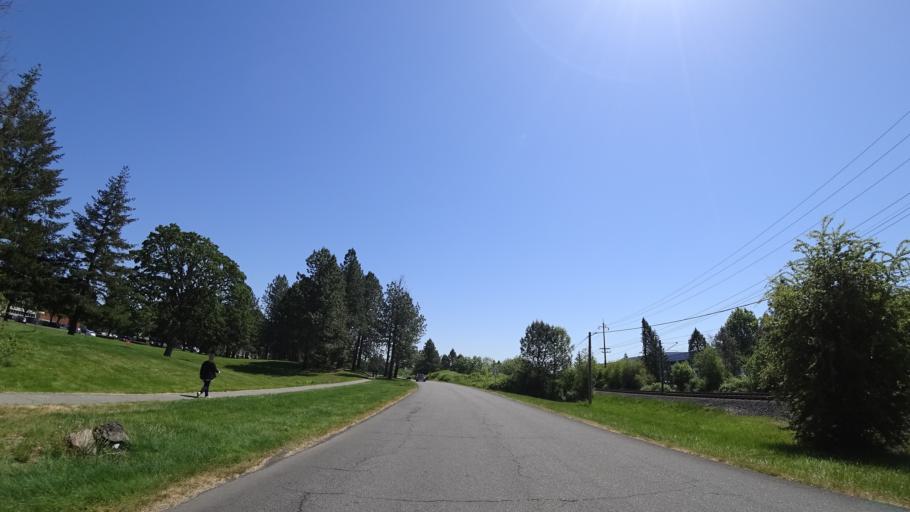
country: US
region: Oregon
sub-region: Washington County
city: Beaverton
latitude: 45.4974
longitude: -122.8264
